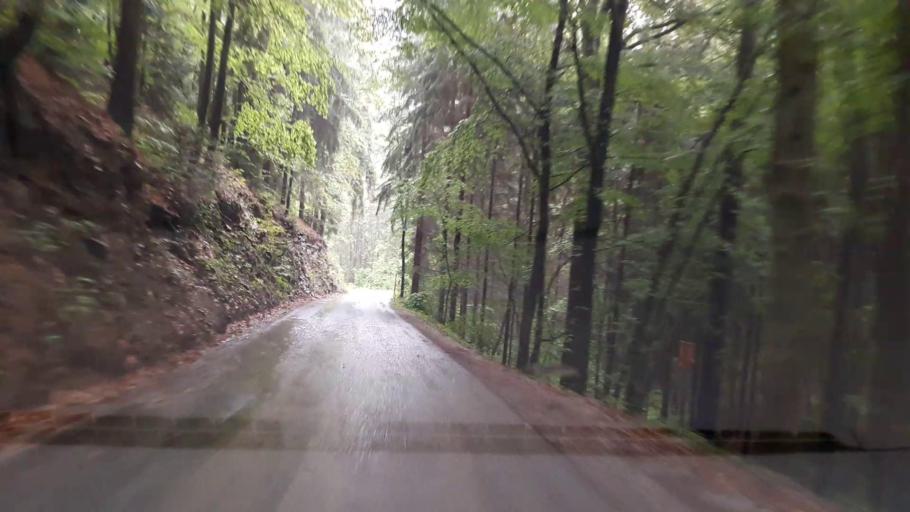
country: AT
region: Lower Austria
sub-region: Politischer Bezirk Krems
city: Aggsbach
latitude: 48.2886
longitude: 15.3762
